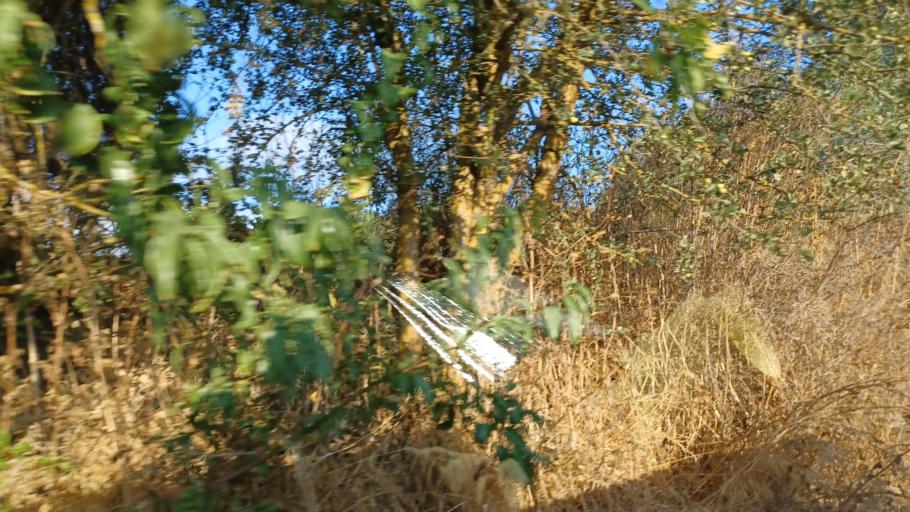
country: CY
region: Pafos
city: Tala
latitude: 34.8850
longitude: 32.4859
